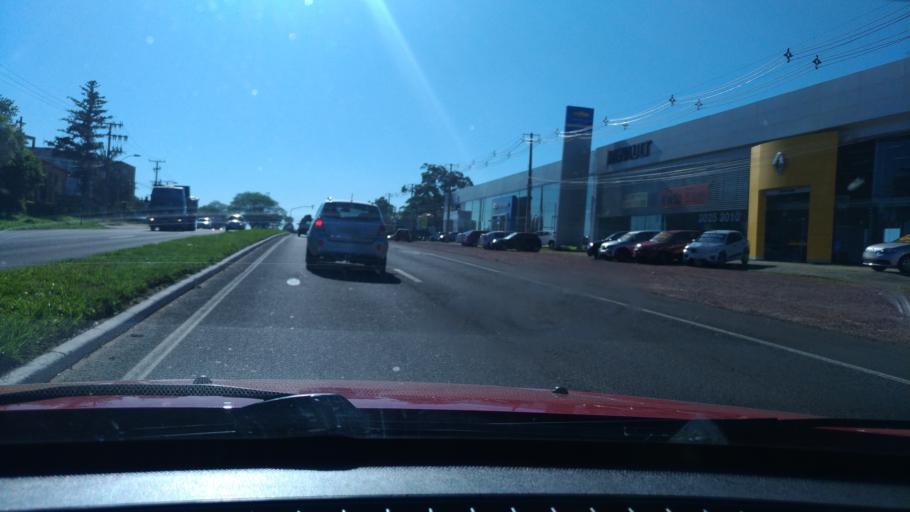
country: BR
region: Rio Grande do Sul
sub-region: Viamao
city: Viamao
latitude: -30.0931
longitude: -51.0743
